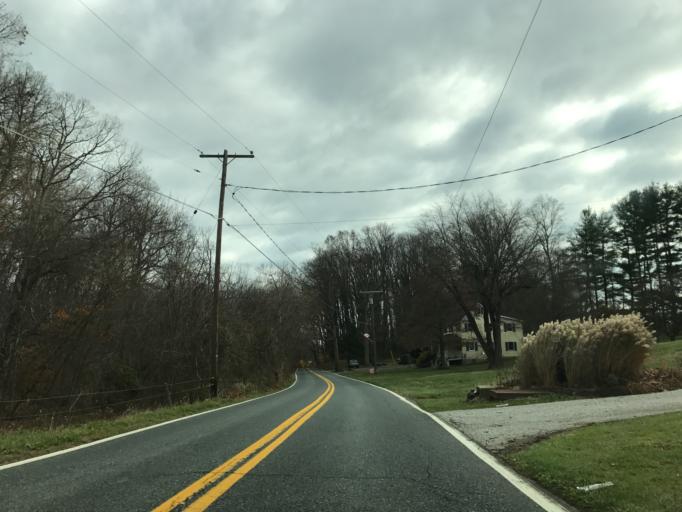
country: US
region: Maryland
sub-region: Baltimore County
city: Perry Hall
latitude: 39.4885
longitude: -76.5146
